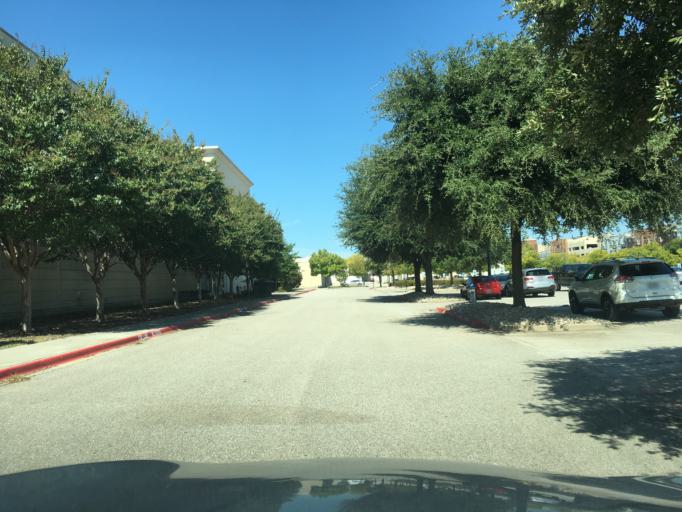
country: US
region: Texas
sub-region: Dallas County
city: Sachse
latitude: 32.9522
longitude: -96.6087
